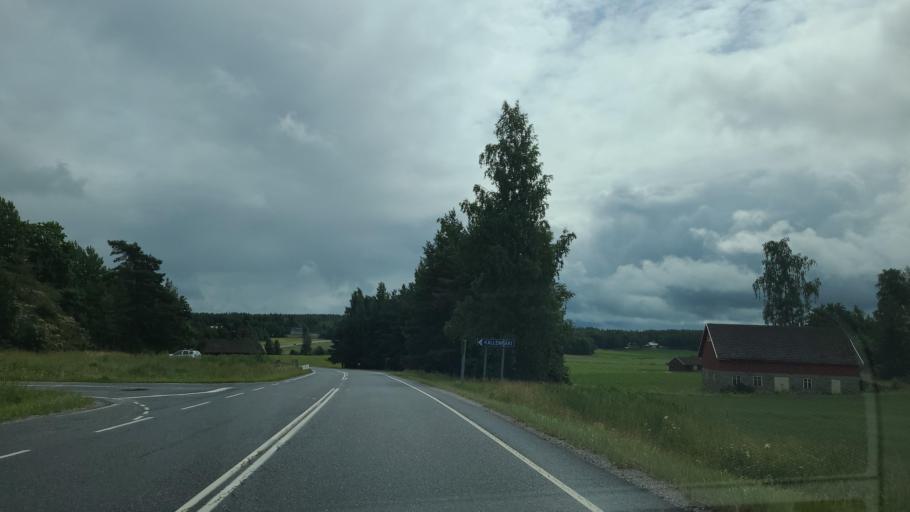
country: FI
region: Varsinais-Suomi
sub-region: Turku
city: Sauvo
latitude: 60.3357
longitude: 22.7041
